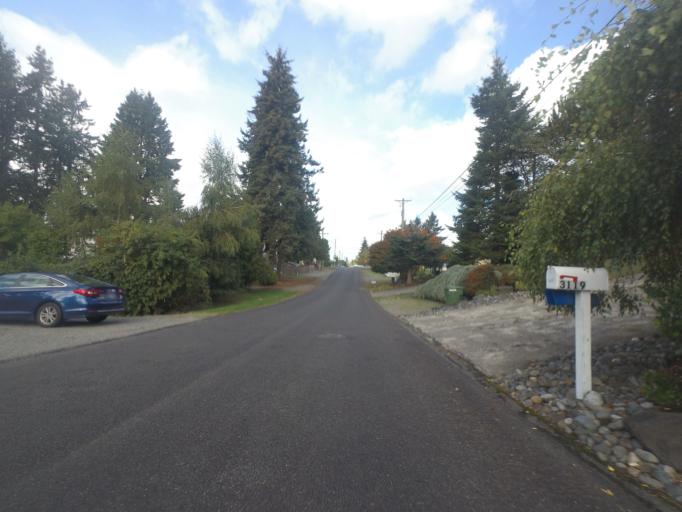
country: US
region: Washington
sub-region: Pierce County
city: University Place
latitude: 47.2308
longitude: -122.5439
